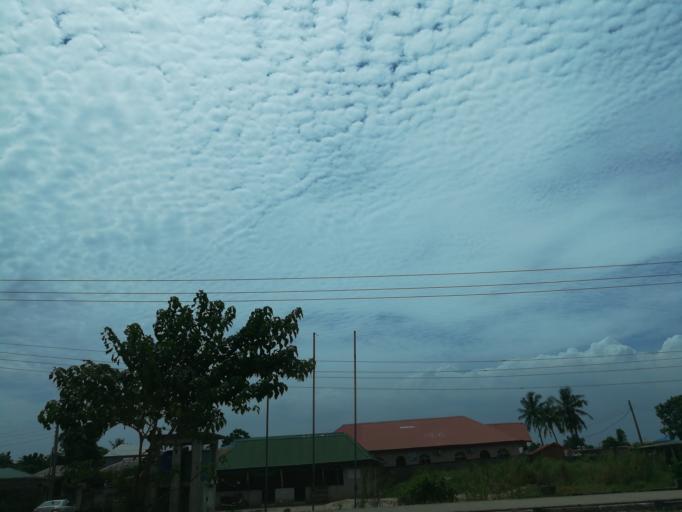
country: NG
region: Lagos
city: Ebute Ikorodu
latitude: 6.5626
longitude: 3.4770
